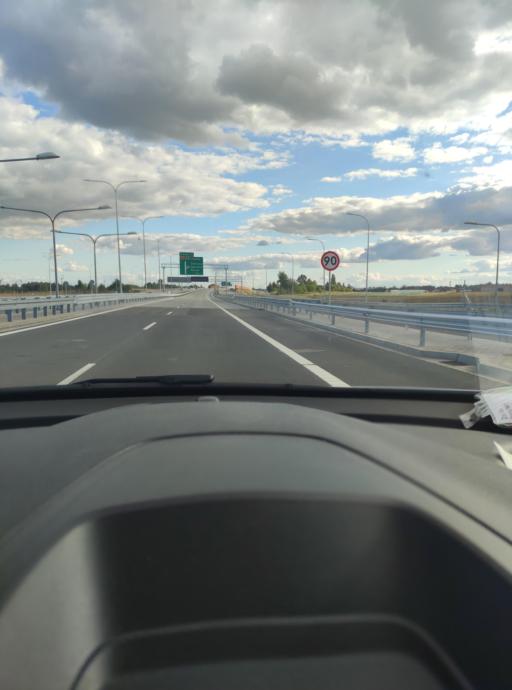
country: PL
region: Masovian Voivodeship
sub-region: Powiat piaseczynski
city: Mysiadlo
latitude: 52.1351
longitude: 20.9889
